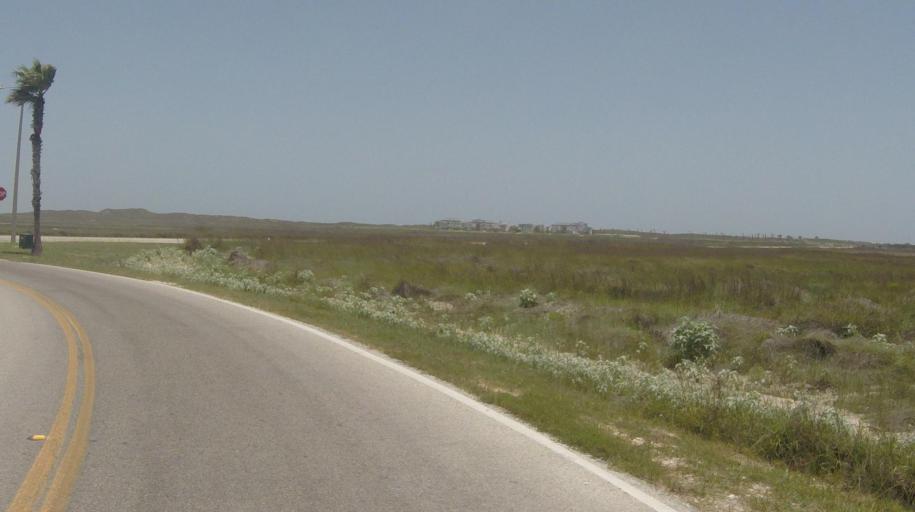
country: US
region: Texas
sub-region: San Patricio County
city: Ingleside
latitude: 27.6207
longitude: -97.2096
